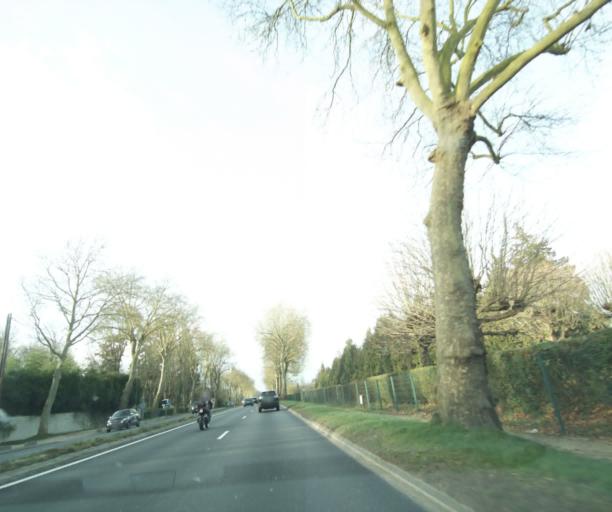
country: FR
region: Ile-de-France
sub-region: Departement des Yvelines
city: Louveciennes
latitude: 48.8521
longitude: 2.1082
